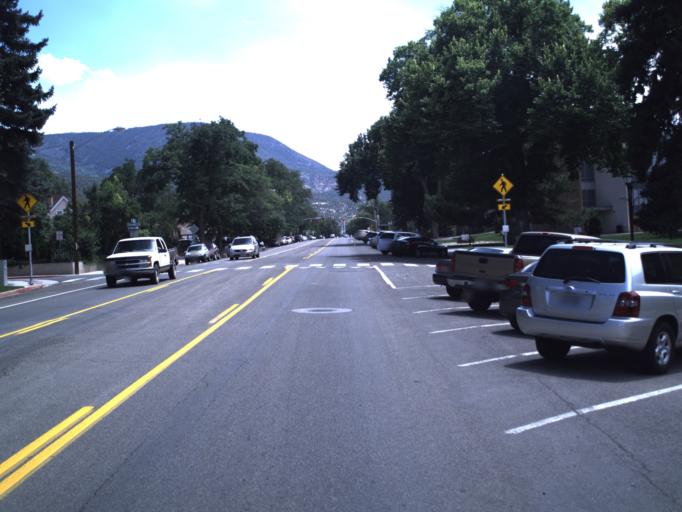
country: US
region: Utah
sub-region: Iron County
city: Cedar City
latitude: 37.6766
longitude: -113.0669
